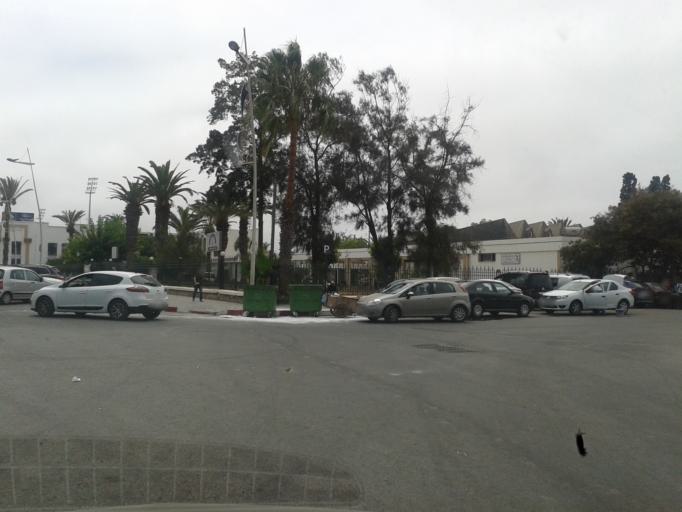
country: MA
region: Souss-Massa-Draa
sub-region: Agadir-Ida-ou-Tnan
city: Agadir
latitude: 30.4180
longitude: -9.5970
